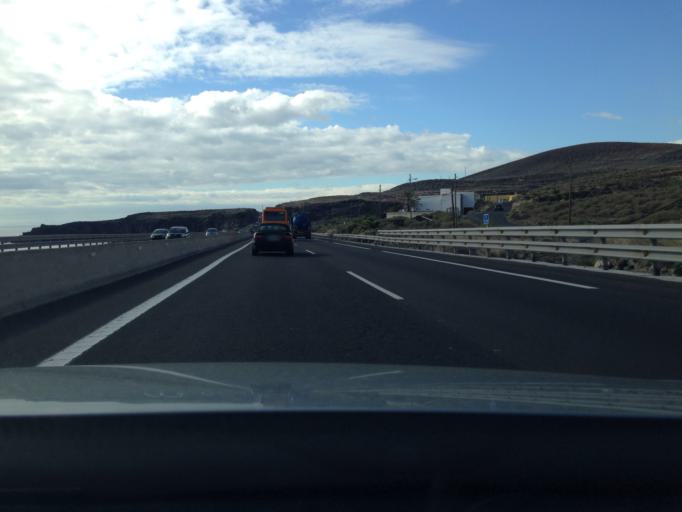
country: ES
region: Canary Islands
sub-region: Provincia de Santa Cruz de Tenerife
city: Fasnia
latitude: 28.1922
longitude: -16.4274
